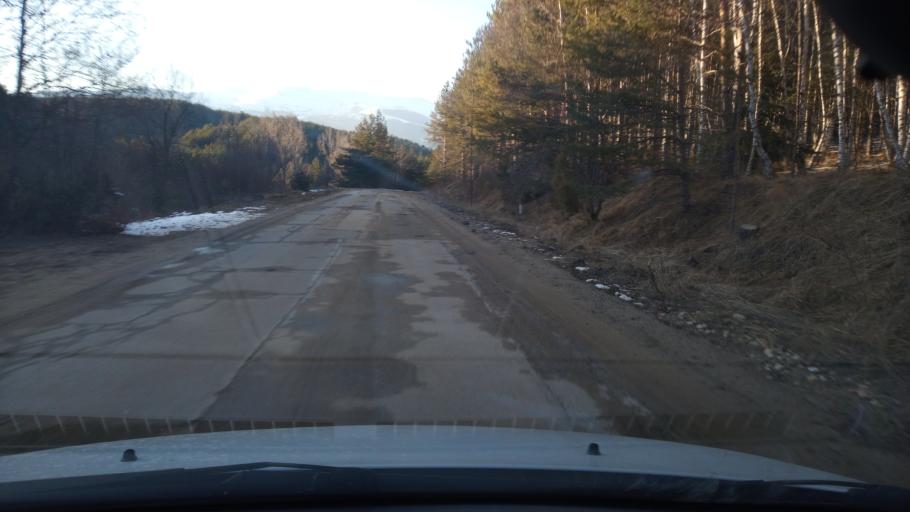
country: BG
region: Sofia-Capital
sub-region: Stolichna Obshtina
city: Sofia
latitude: 42.4852
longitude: 23.3859
